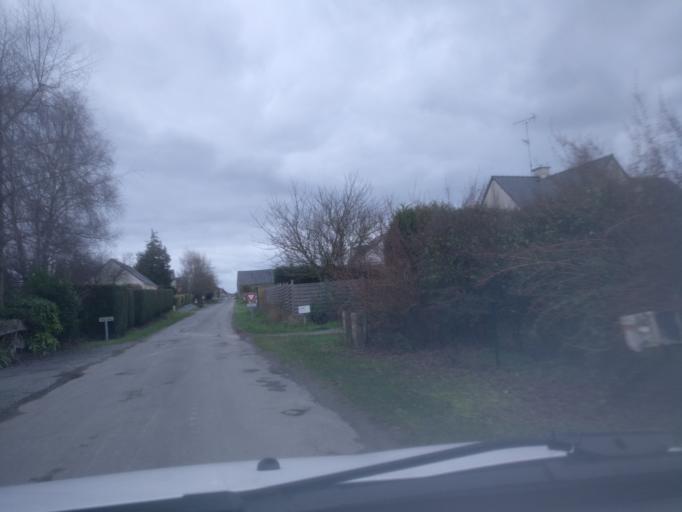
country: FR
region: Lower Normandy
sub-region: Departement de la Manche
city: Marcey-les-Greves
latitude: 48.6730
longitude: -1.4092
